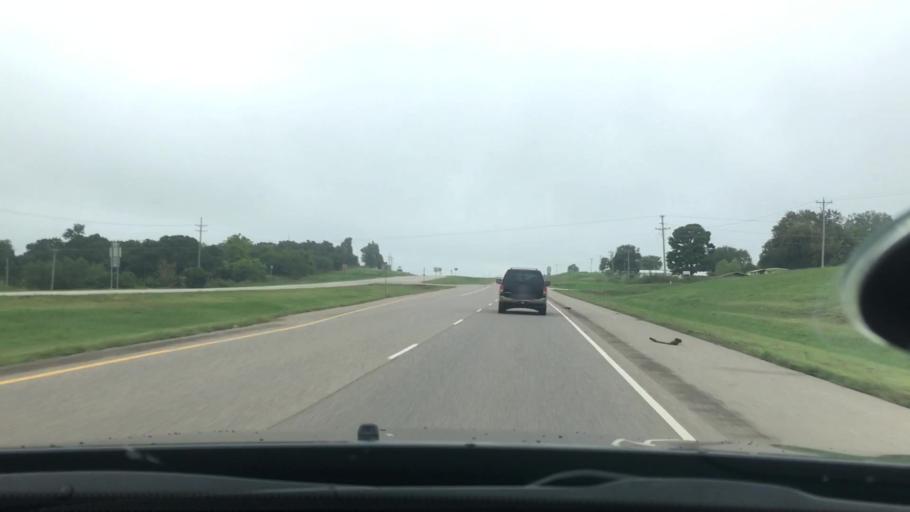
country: US
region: Oklahoma
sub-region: Seminole County
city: Seminole
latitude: 35.3030
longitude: -96.6707
